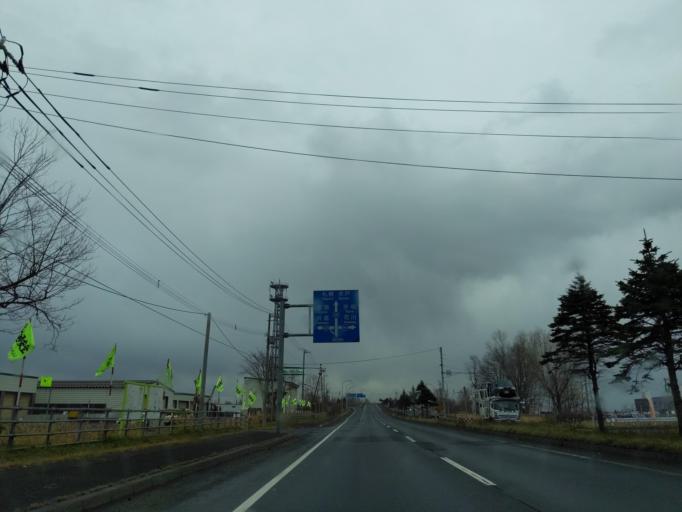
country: JP
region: Hokkaido
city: Ishikari
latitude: 43.1852
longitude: 141.3171
